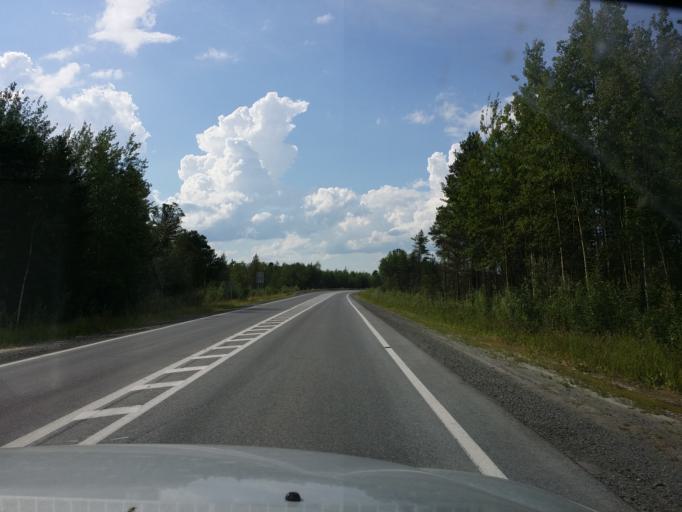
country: RU
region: Khanty-Mansiyskiy Avtonomnyy Okrug
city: Megion
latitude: 61.1313
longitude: 75.7751
